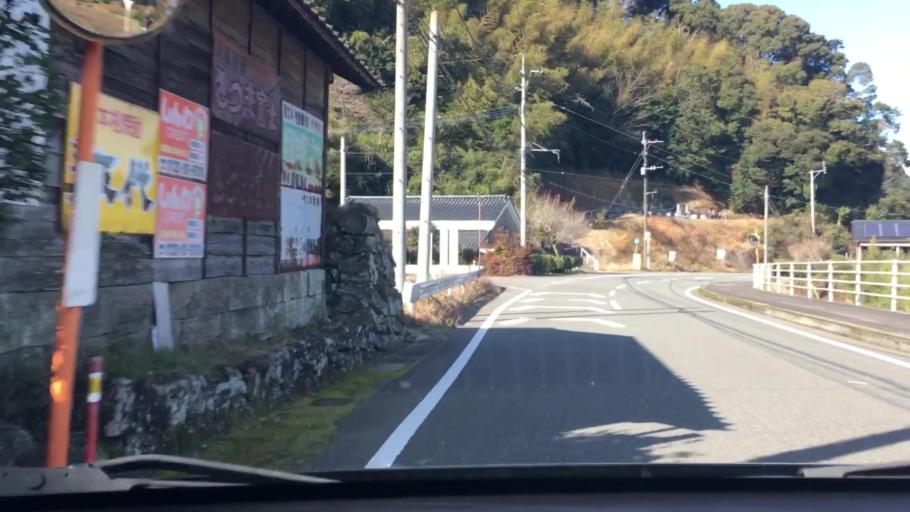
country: JP
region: Kagoshima
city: Ijuin
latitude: 31.7422
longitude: 130.4096
